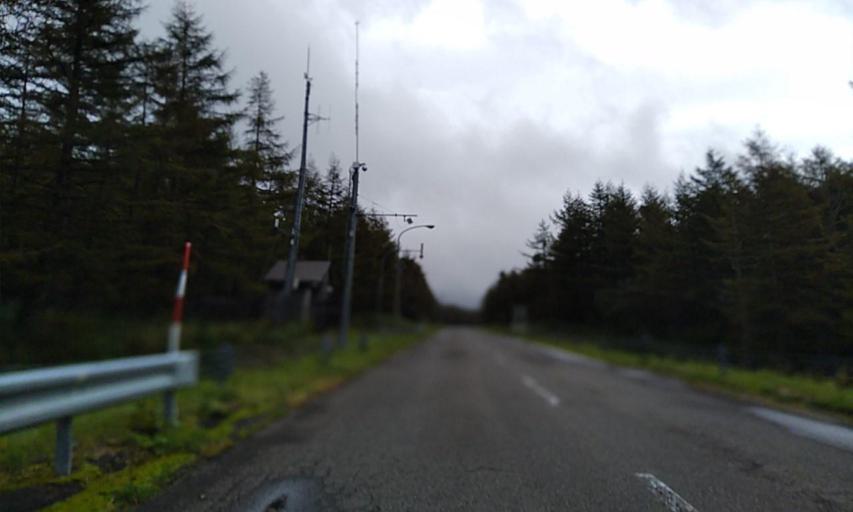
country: JP
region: Hokkaido
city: Abashiri
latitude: 43.6102
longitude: 144.6020
